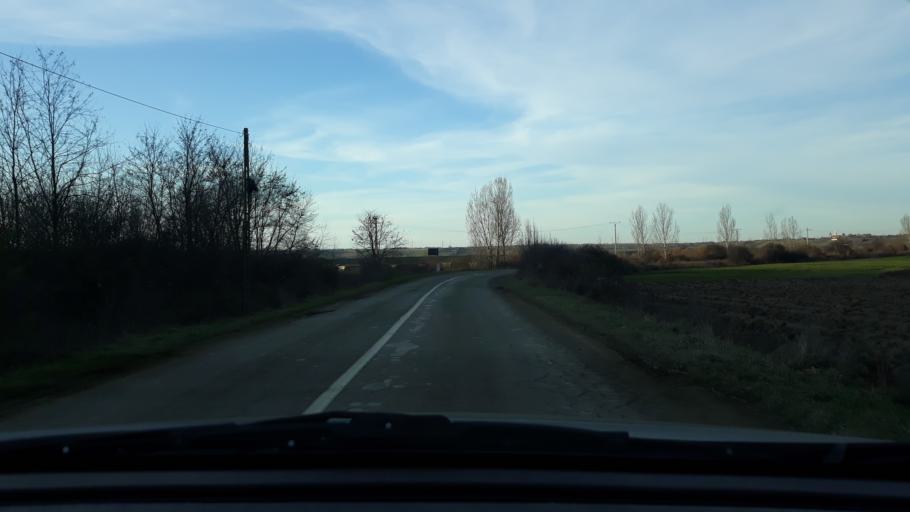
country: RO
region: Bihor
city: Foglas
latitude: 47.2332
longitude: 22.5384
